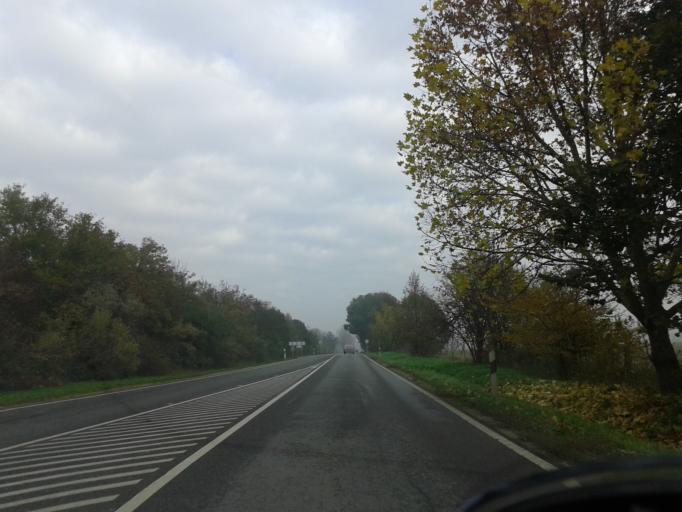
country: HU
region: Pest
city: Szazhalombatta
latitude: 47.3504
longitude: 18.9036
